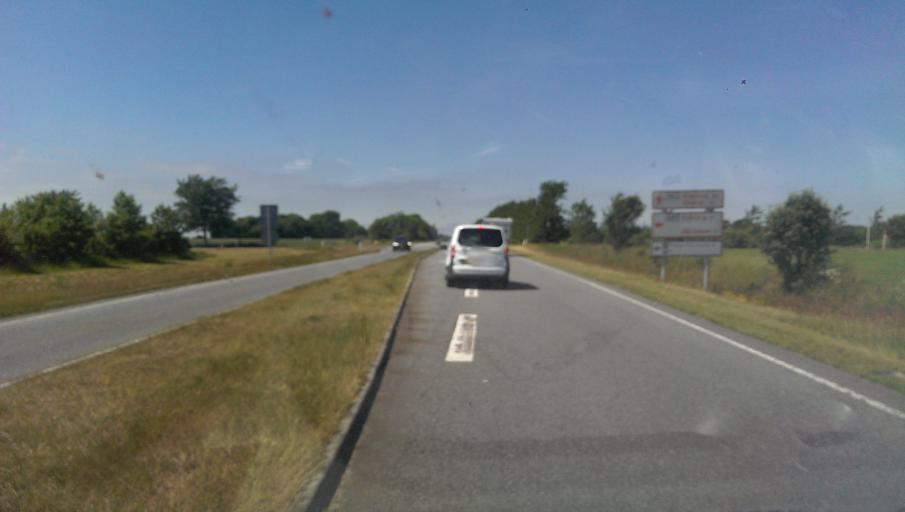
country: DK
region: South Denmark
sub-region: Esbjerg Kommune
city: Esbjerg
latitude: 55.5355
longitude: 8.4174
